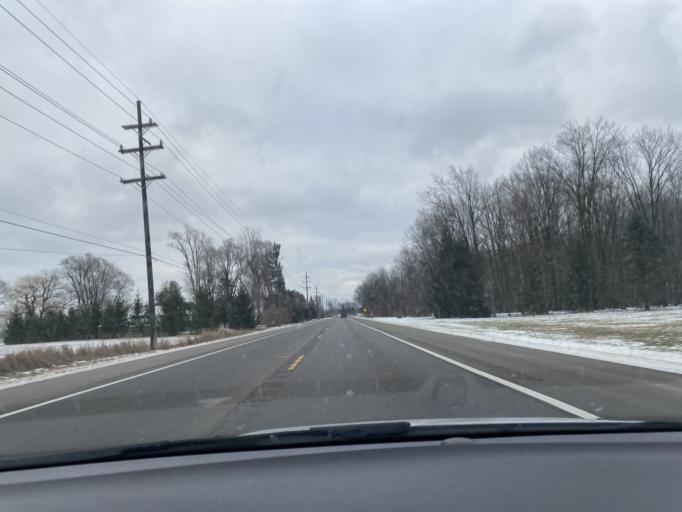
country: US
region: Michigan
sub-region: Lapeer County
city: Imlay City
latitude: 42.9827
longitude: -83.0625
